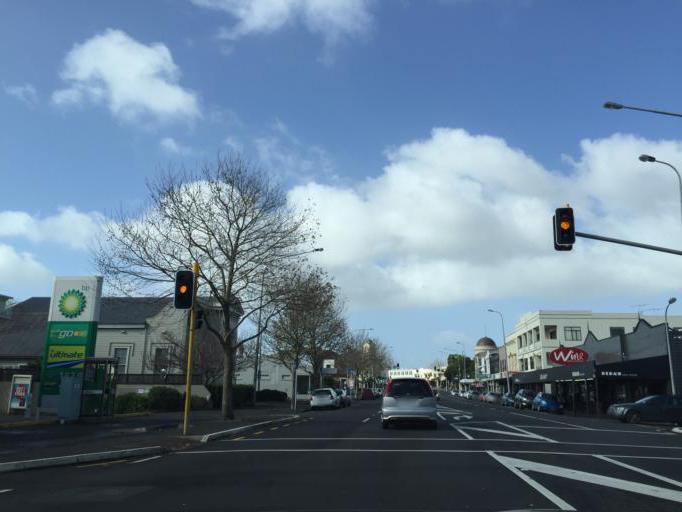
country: NZ
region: Auckland
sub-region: Auckland
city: Auckland
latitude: -36.8460
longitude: 174.7419
